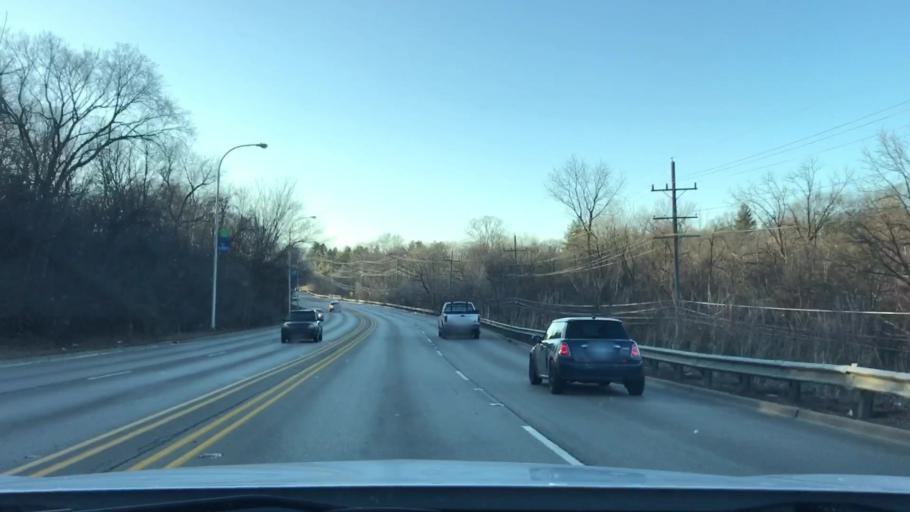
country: US
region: Illinois
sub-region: Kane County
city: Elgin
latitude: 42.0586
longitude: -88.3009
